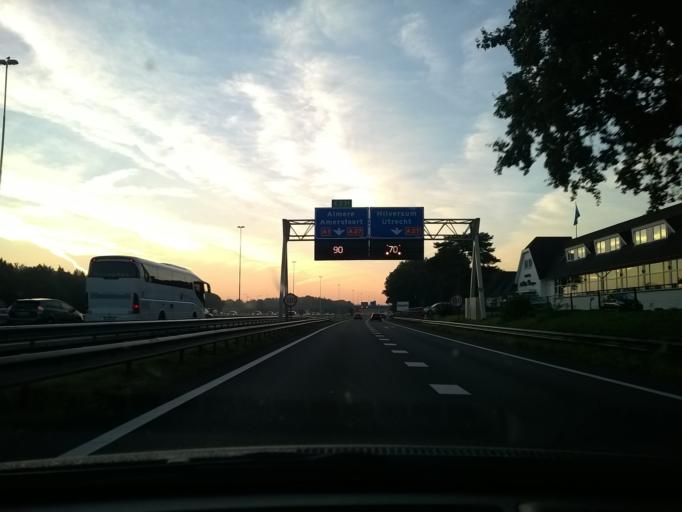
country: NL
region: North Holland
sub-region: Gemeente Laren
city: Laren
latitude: 52.2360
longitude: 5.2321
